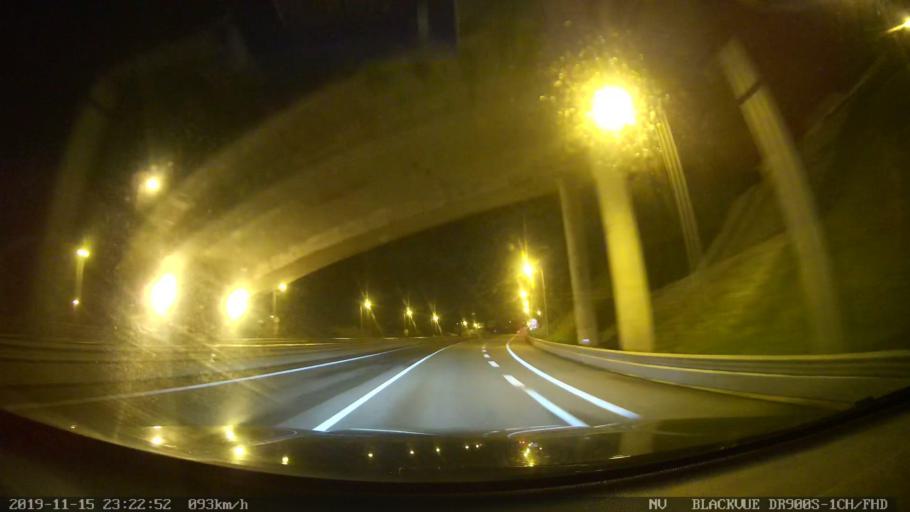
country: PT
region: Porto
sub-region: Amarante
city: Amarante
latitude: 41.2610
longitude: -8.0751
